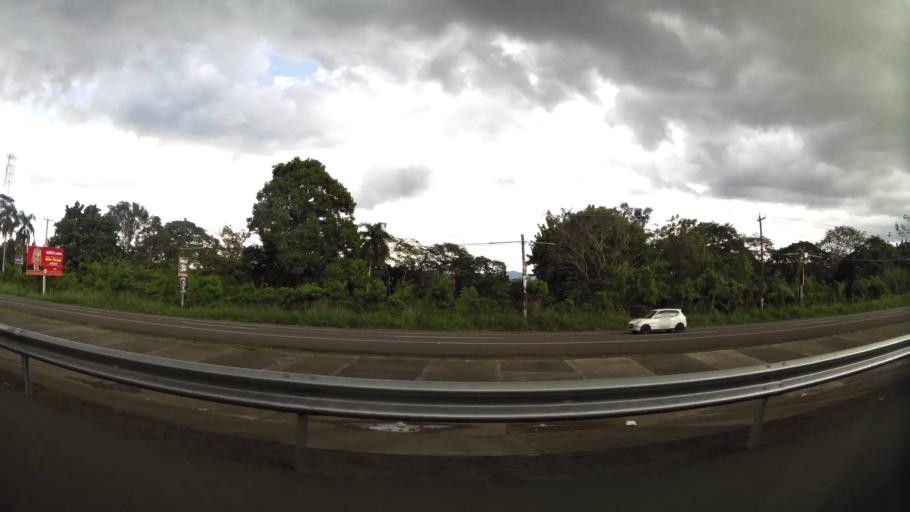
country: DO
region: Monsenor Nouel
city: Sabana del Puerto
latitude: 19.0205
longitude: -70.4458
